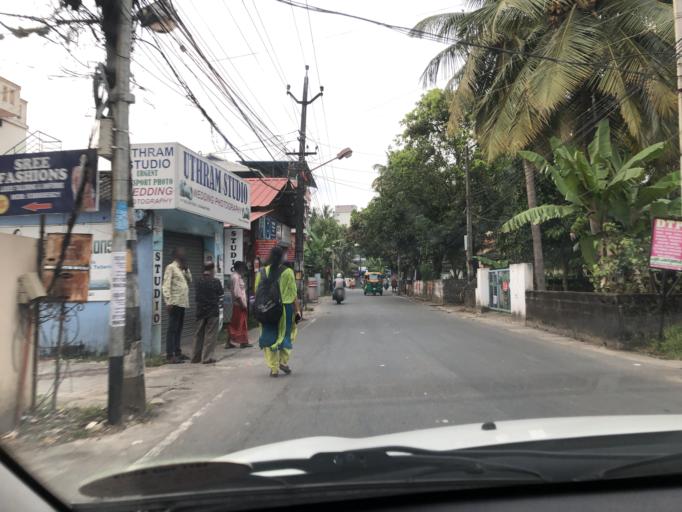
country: IN
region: Kerala
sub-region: Ernakulam
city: Cochin
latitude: 9.9603
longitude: 76.3014
